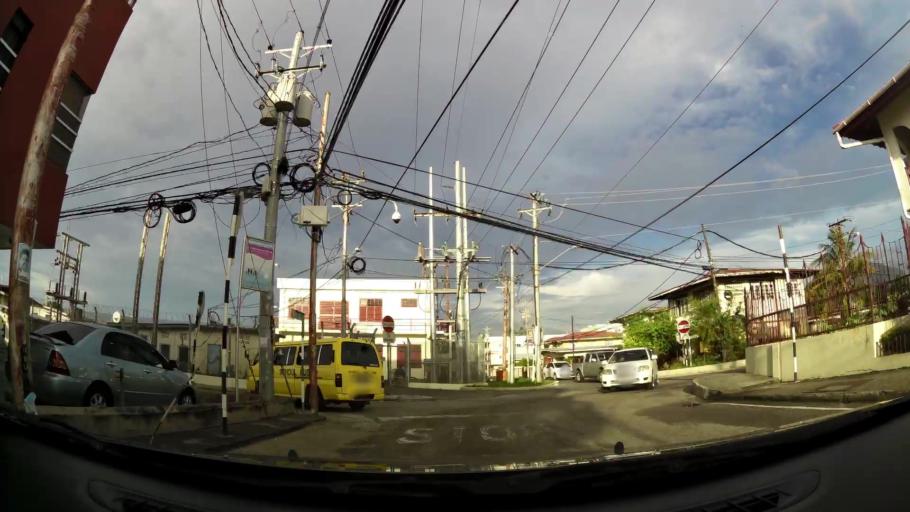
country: TT
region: Tunapuna/Piarco
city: Tunapuna
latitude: 10.6385
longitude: -61.4028
